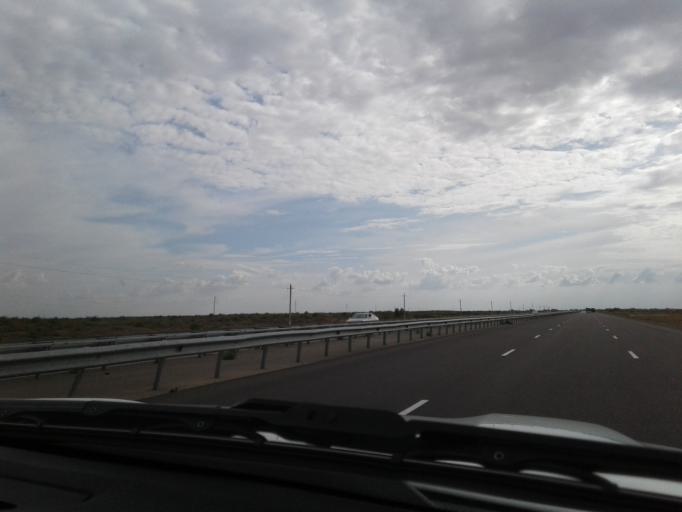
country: TM
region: Mary
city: Mary
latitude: 37.4588
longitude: 61.6655
